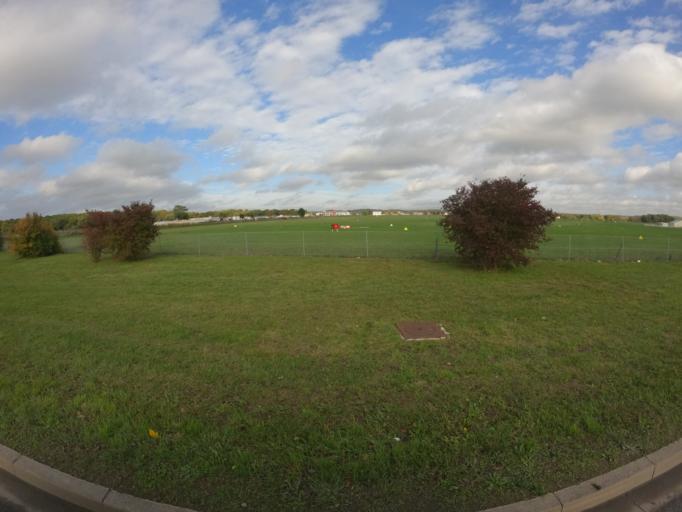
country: FR
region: Ile-de-France
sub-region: Departement de Seine-et-Marne
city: Chelles
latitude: 48.8936
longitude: 2.6038
